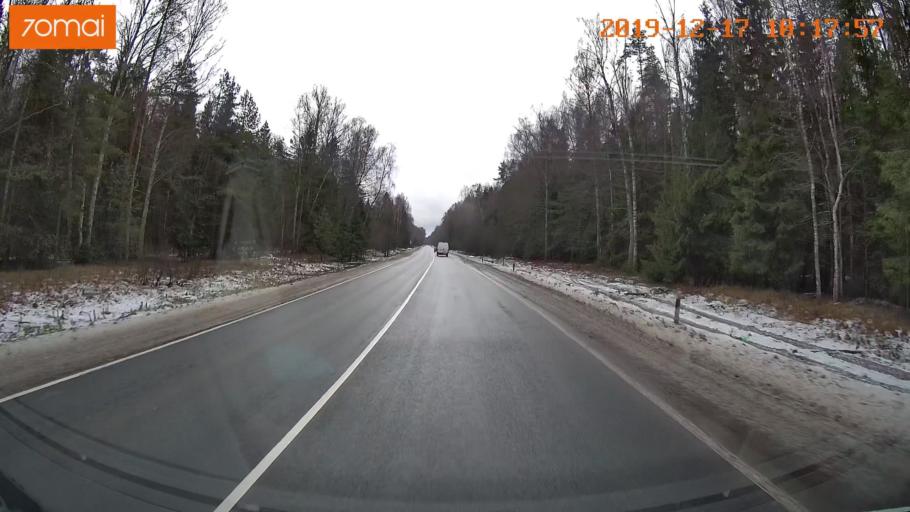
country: RU
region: Vladimir
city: Anopino
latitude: 55.7762
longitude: 40.6740
